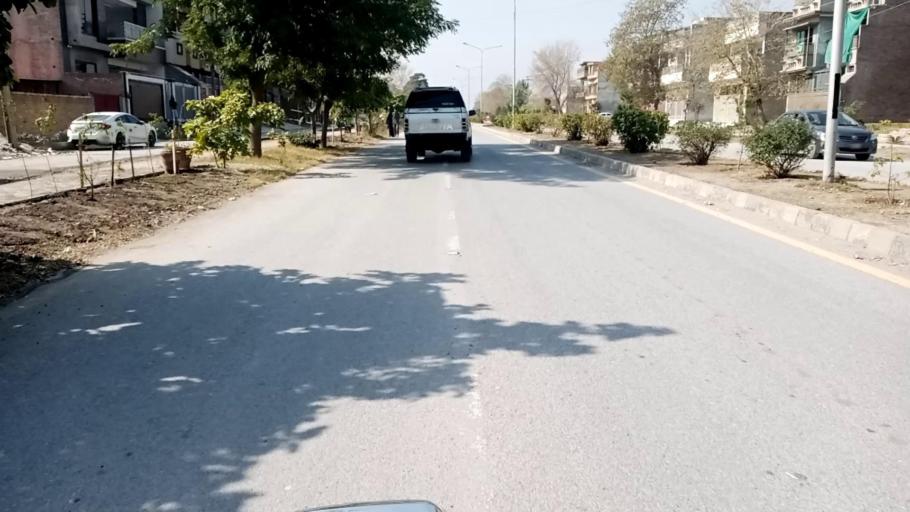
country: PK
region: Khyber Pakhtunkhwa
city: Peshawar
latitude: 33.9626
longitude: 71.4164
